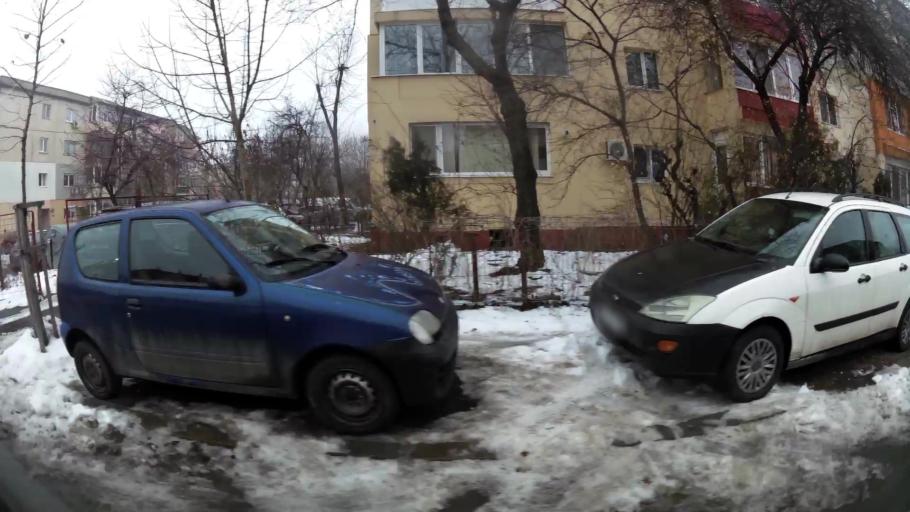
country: RO
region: Ilfov
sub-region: Comuna Chiajna
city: Rosu
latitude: 44.4409
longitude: 26.0055
